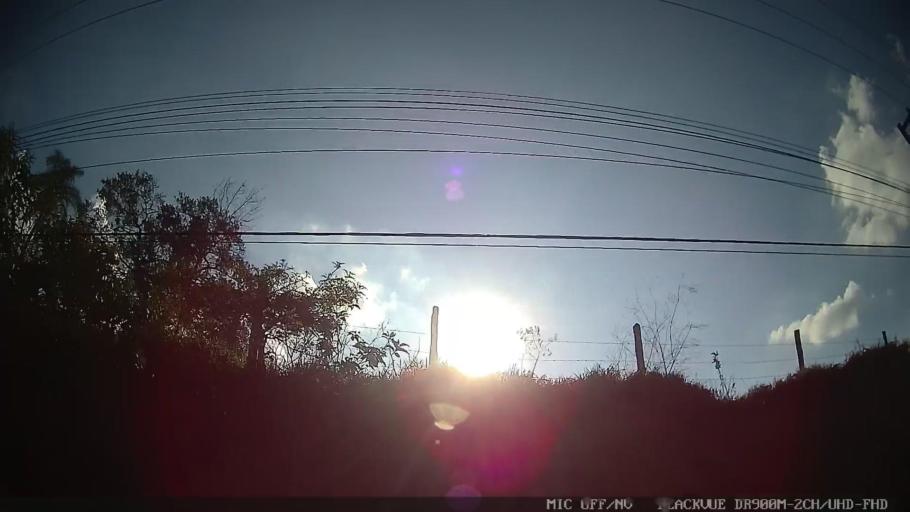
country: BR
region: Sao Paulo
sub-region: Braganca Paulista
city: Braganca Paulista
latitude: -22.9689
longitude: -46.5105
